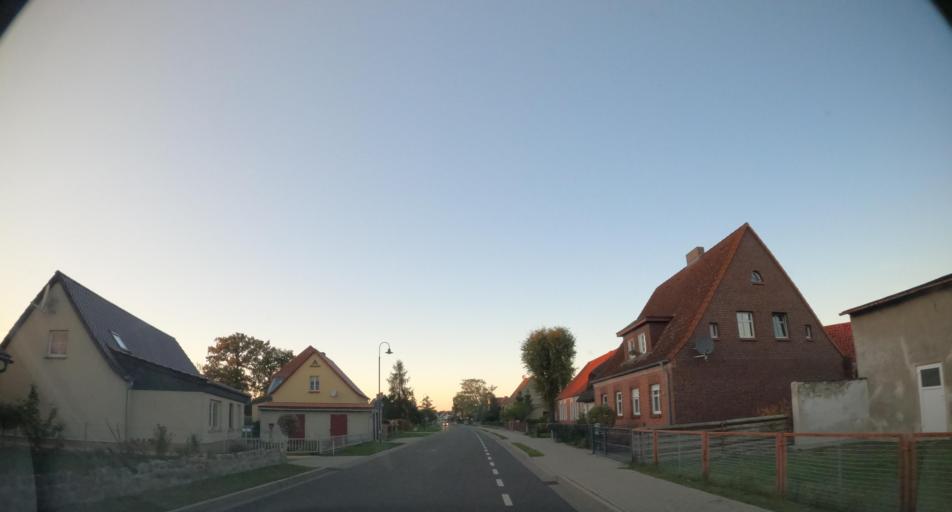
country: DE
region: Mecklenburg-Vorpommern
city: Ueckermunde
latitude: 53.7560
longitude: 14.0156
